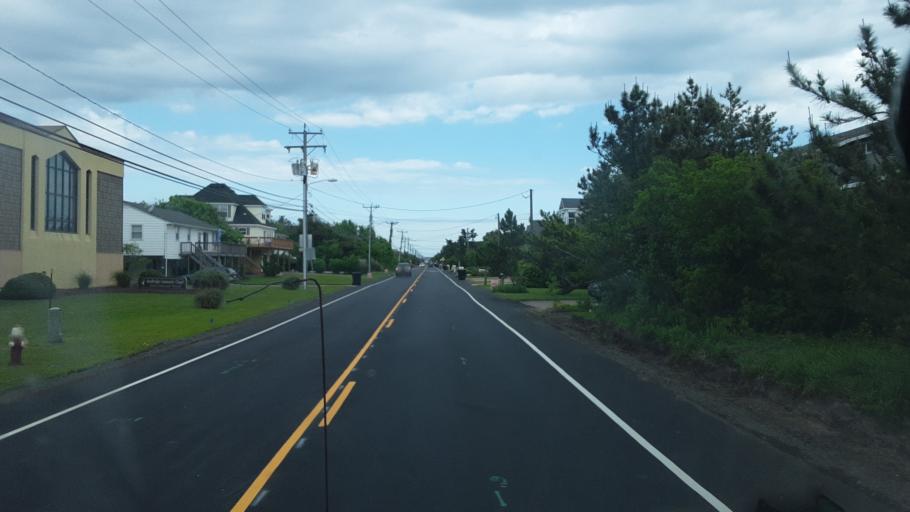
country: US
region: Virginia
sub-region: City of Virginia Beach
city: Virginia Beach
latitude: 36.7226
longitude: -75.9363
